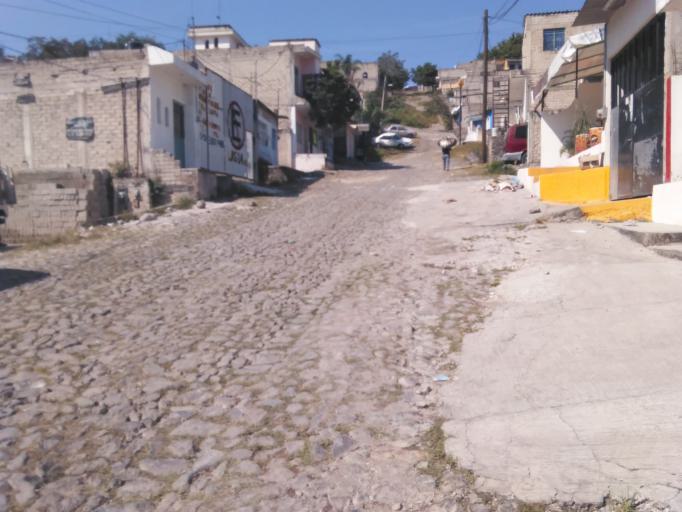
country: MX
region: Nayarit
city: Tepic
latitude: 21.5221
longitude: -104.9081
